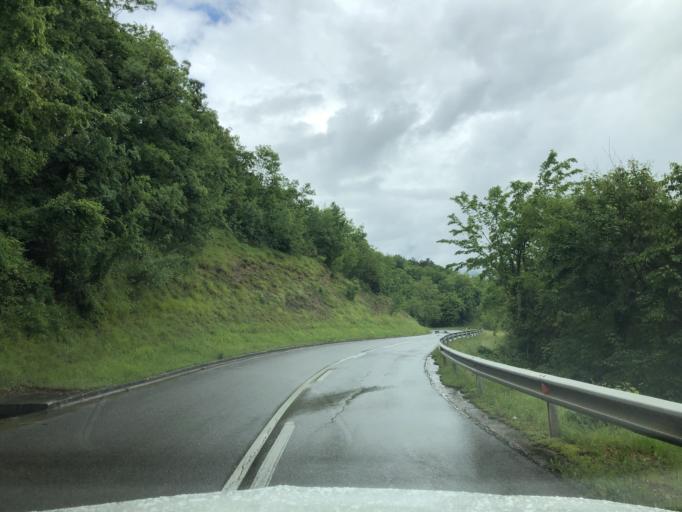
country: SI
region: Koper-Capodistria
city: Prade
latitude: 45.5069
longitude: 13.7752
